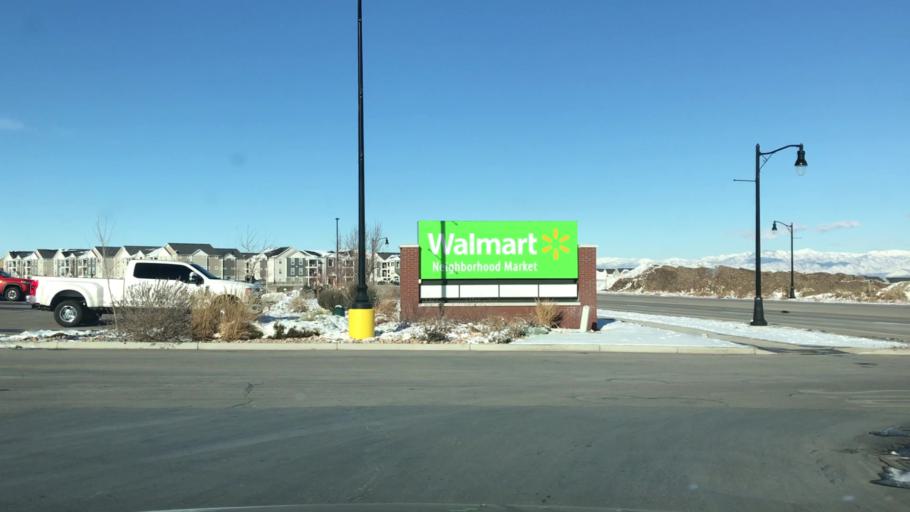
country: US
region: Utah
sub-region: Salt Lake County
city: Herriman
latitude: 40.5087
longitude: -112.0105
